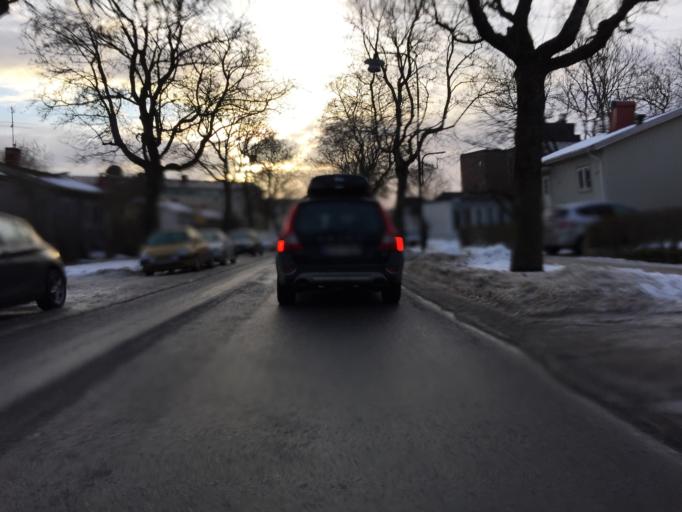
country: SE
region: Stockholm
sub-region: Stockholms Kommun
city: Bromma
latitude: 59.3439
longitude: 17.9223
